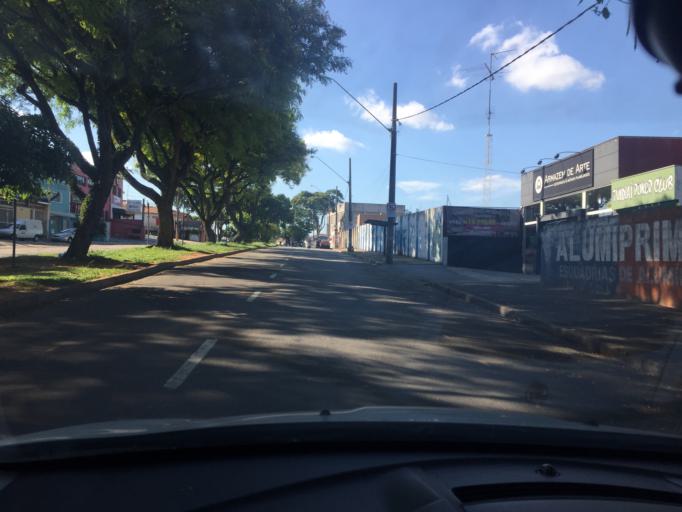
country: BR
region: Sao Paulo
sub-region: Jundiai
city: Jundiai
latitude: -23.2103
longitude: -46.8651
